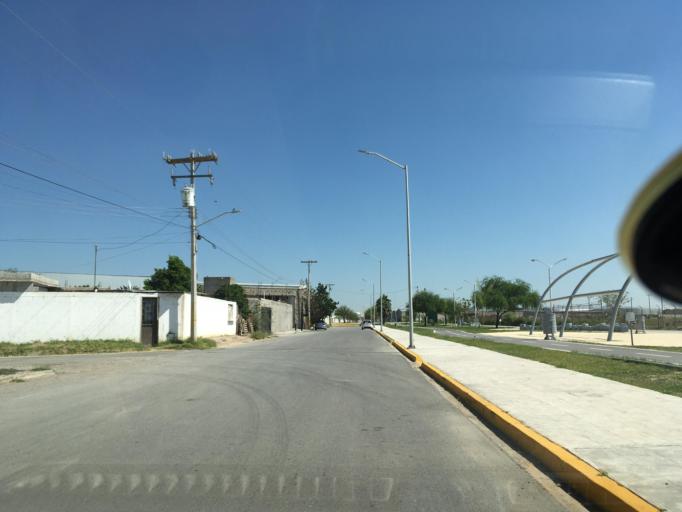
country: MX
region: Coahuila
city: Torreon
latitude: 25.5249
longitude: -103.3772
